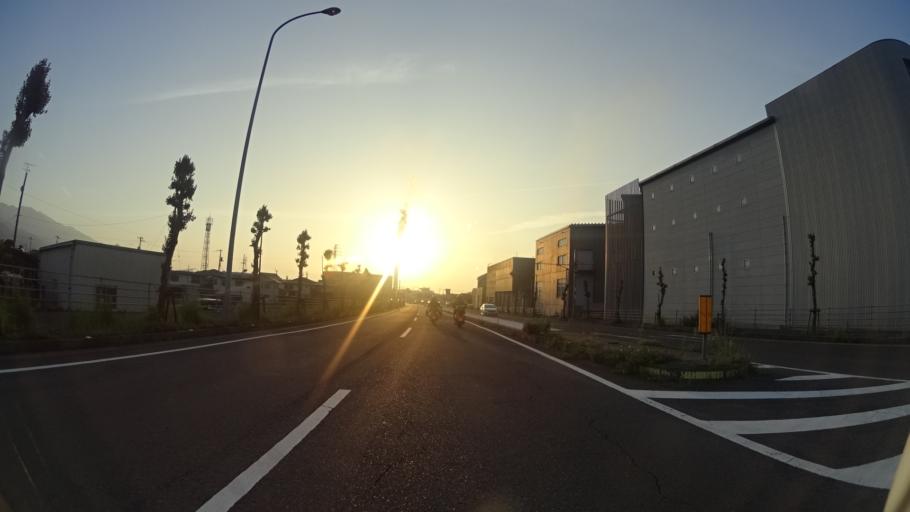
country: JP
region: Ehime
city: Kawanoecho
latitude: 33.9868
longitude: 133.5675
